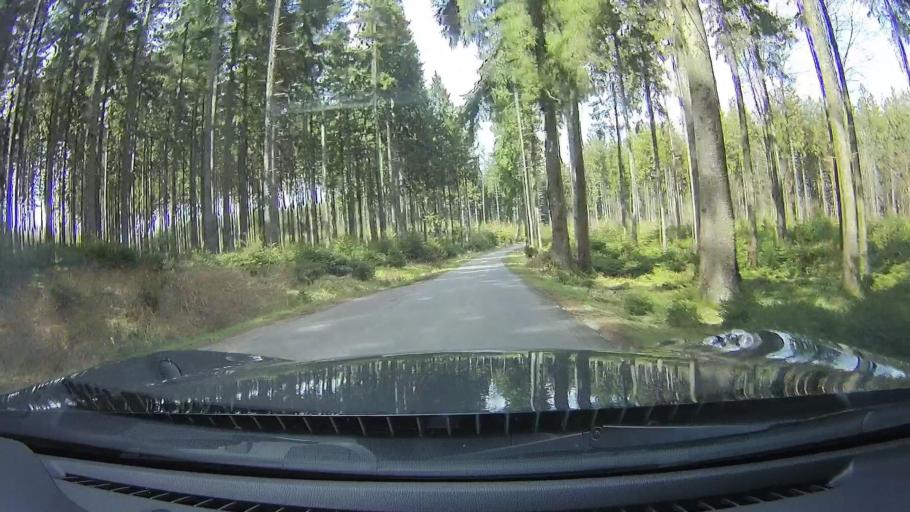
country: DE
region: Hesse
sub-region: Regierungsbezirk Darmstadt
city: Hesseneck
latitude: 49.5911
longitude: 9.0875
